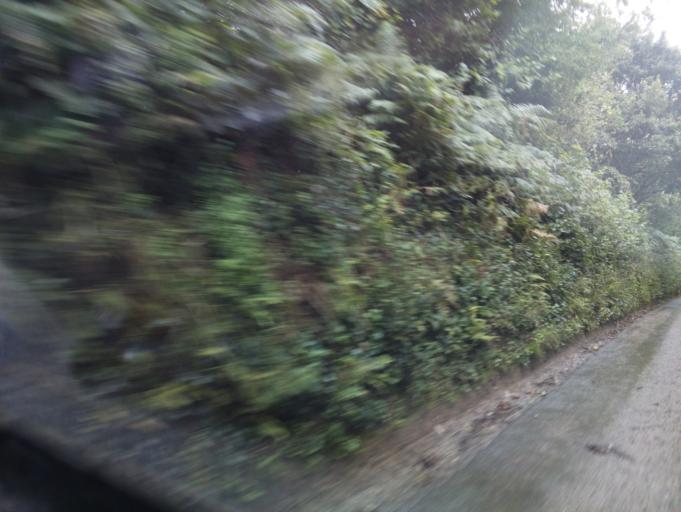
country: GB
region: England
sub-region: Devon
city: Totnes
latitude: 50.3416
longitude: -3.6845
